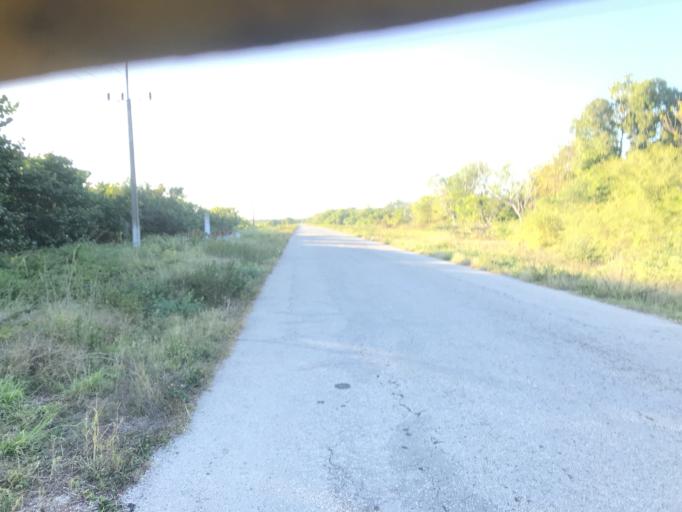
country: CU
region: Cienfuegos
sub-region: Municipio de Aguada de Pasajeros
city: Aguada de Pasajeros
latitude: 22.0786
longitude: -81.0684
